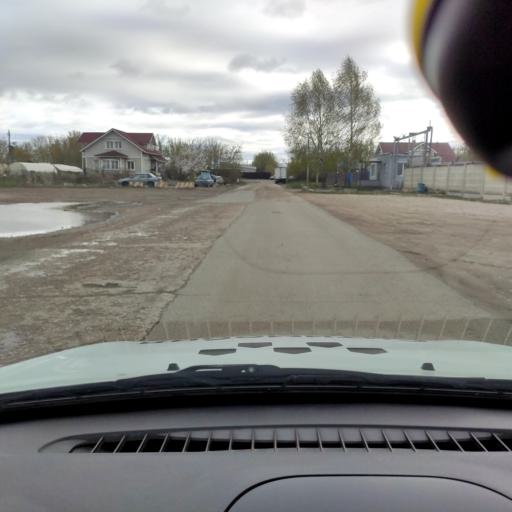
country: RU
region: Samara
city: Tol'yatti
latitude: 53.5780
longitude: 49.3131
